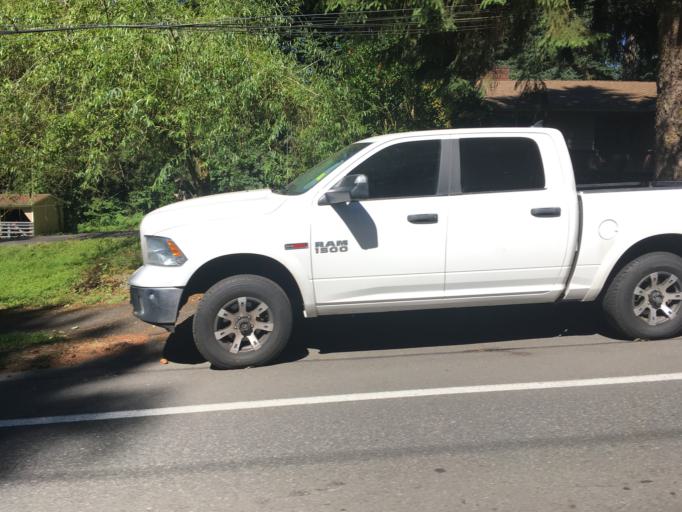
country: US
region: Washington
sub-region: King County
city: Bellevue
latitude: 47.6326
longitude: -122.1621
